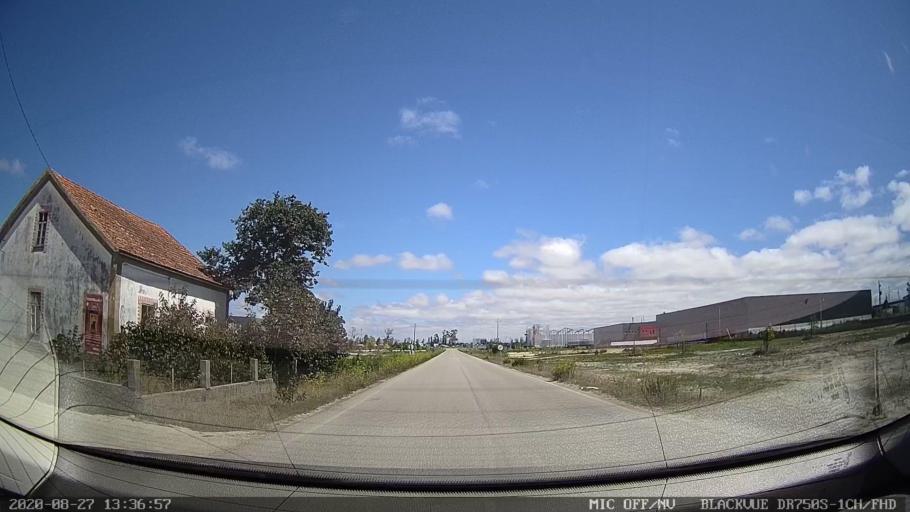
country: PT
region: Coimbra
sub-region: Mira
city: Mira
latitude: 40.4558
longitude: -8.7092
